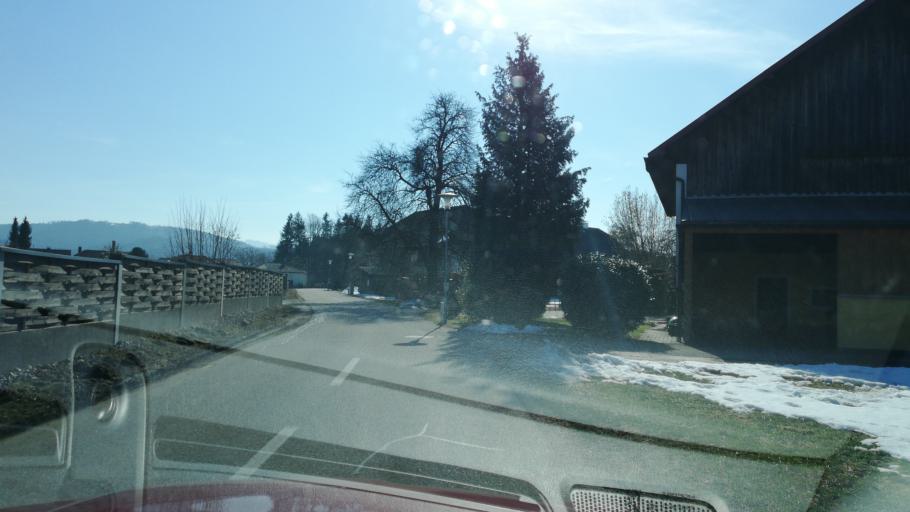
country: AT
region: Upper Austria
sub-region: Politischer Bezirk Vocklabruck
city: Lenzing
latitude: 47.9707
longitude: 13.6221
